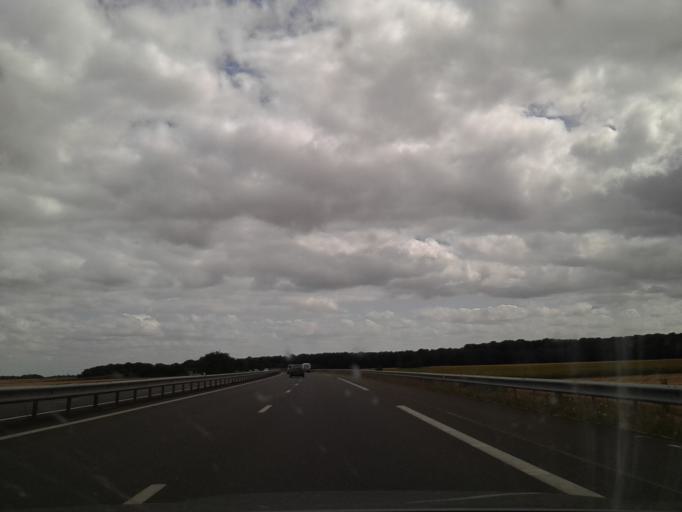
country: FR
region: Centre
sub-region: Departement du Cher
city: Levet
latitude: 46.9451
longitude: 2.4166
